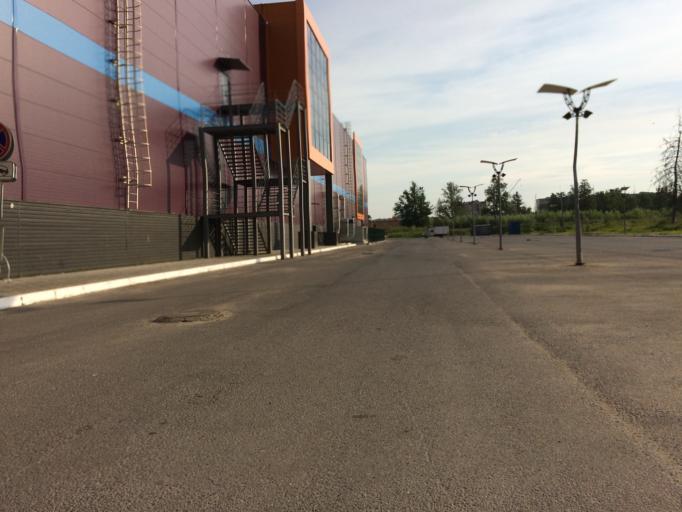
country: RU
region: Mariy-El
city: Yoshkar-Ola
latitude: 56.6276
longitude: 47.9308
